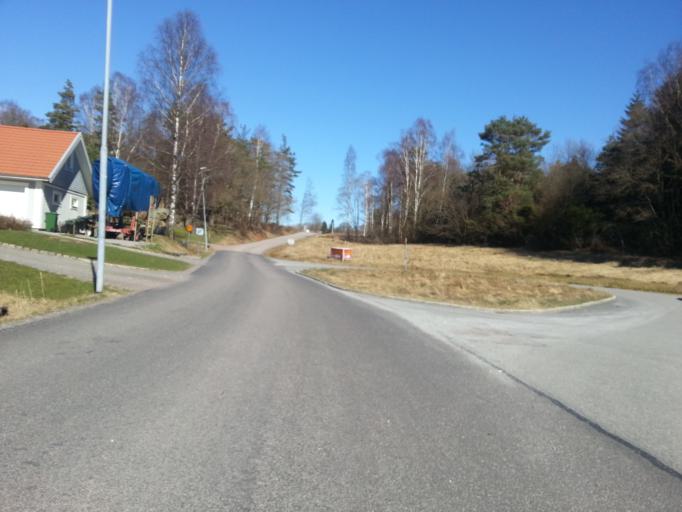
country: SE
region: Vaestra Goetaland
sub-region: Kungalvs Kommun
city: Kungalv
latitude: 57.8943
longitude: 11.9721
